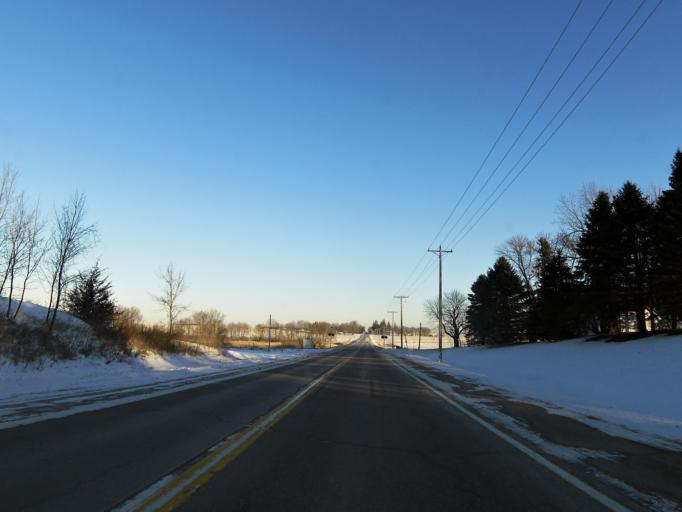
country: US
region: Minnesota
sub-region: Rice County
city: Northfield
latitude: 44.5438
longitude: -93.1987
